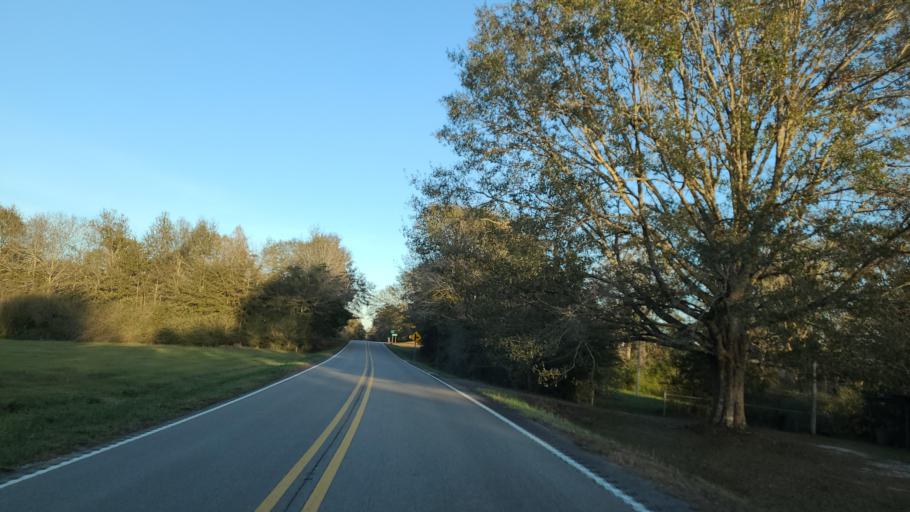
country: US
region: Mississippi
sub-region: Lamar County
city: Lumberton
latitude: 30.9998
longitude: -89.3437
